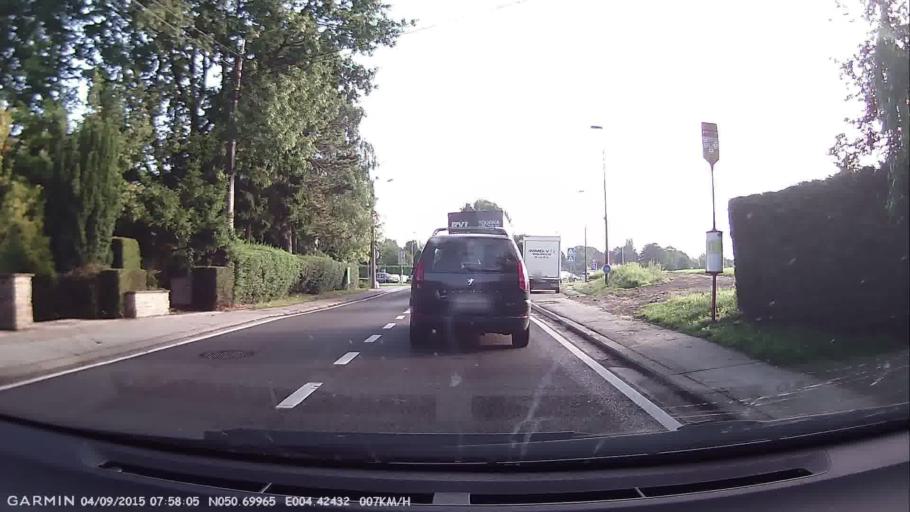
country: BE
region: Wallonia
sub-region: Province du Brabant Wallon
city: Waterloo
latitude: 50.6997
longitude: 4.4244
